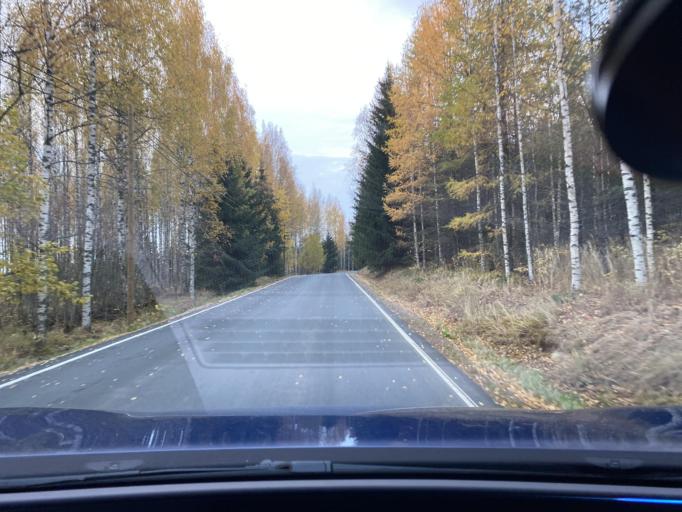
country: FI
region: Varsinais-Suomi
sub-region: Loimaa
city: Alastaro
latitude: 61.0888
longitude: 22.9117
